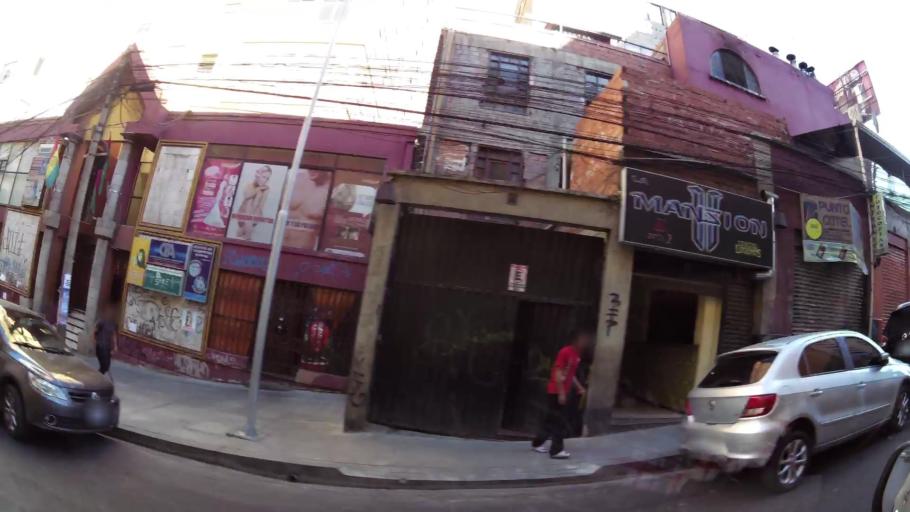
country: BO
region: La Paz
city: La Paz
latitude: -16.5036
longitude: -68.1307
